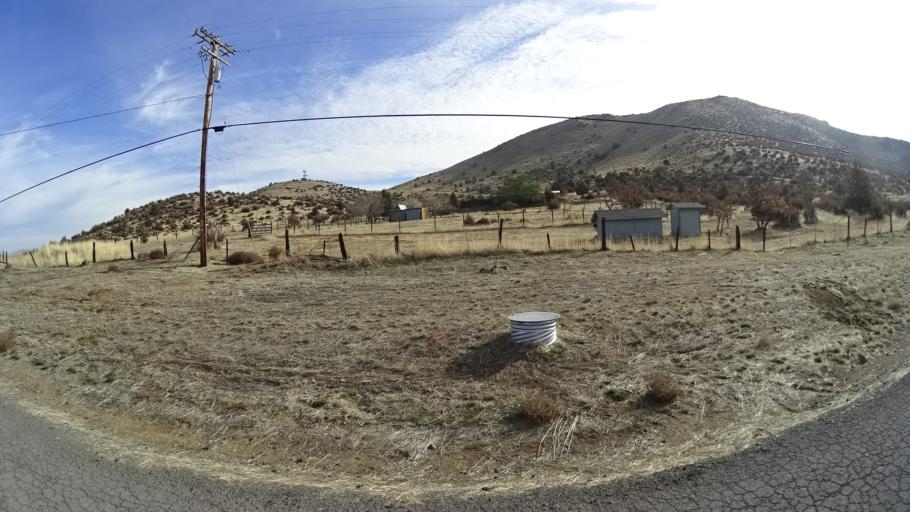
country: US
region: California
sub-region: Siskiyou County
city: Montague
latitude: 41.7180
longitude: -122.5213
